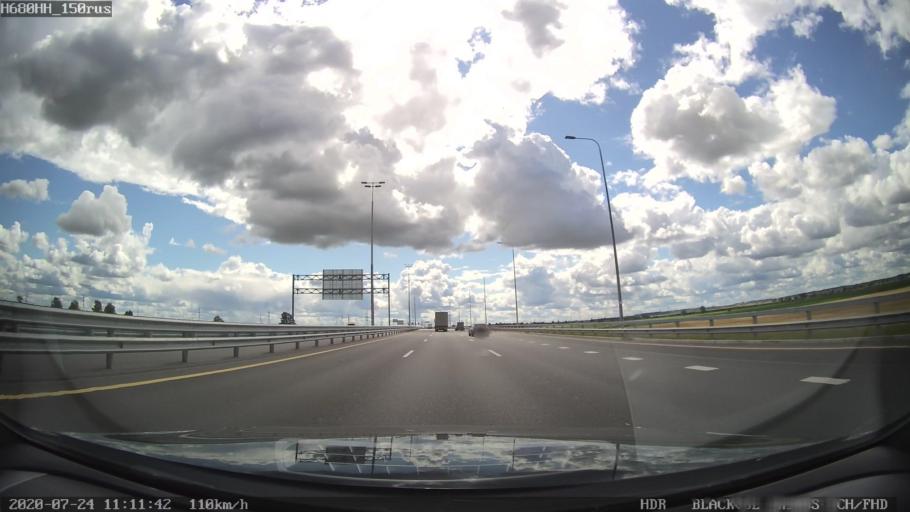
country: RU
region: Leningrad
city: Fedorovskoye
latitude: 59.7189
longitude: 30.5201
